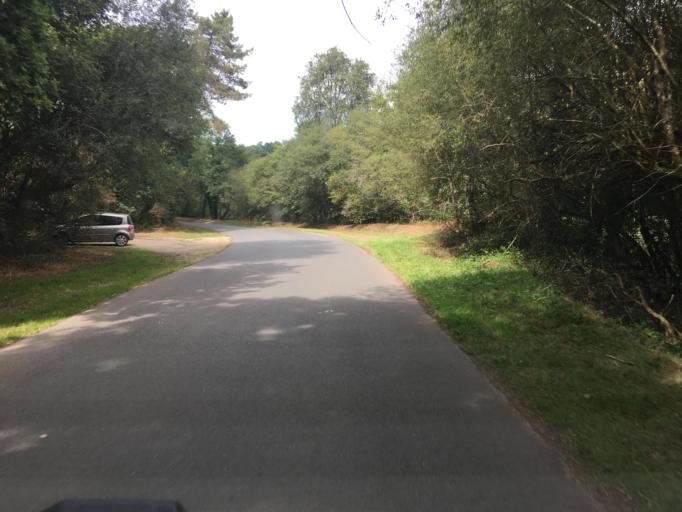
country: FR
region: Brittany
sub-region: Departement des Cotes-d'Armor
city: Gouarec
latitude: 48.2067
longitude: -3.1158
